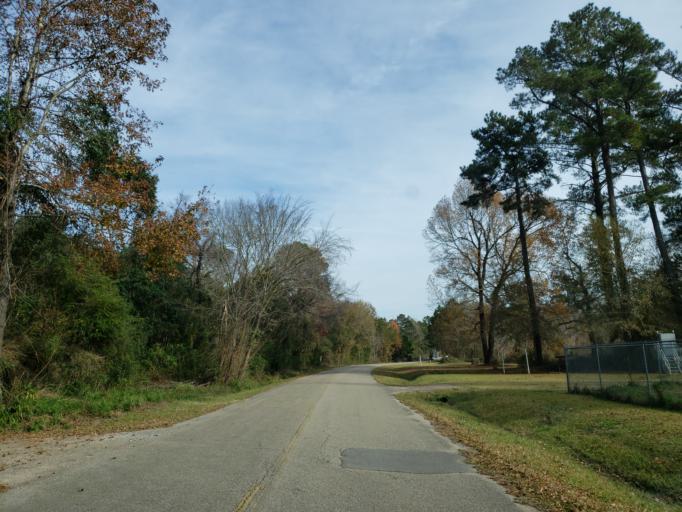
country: US
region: Mississippi
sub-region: Forrest County
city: Glendale
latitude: 31.3537
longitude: -89.3305
